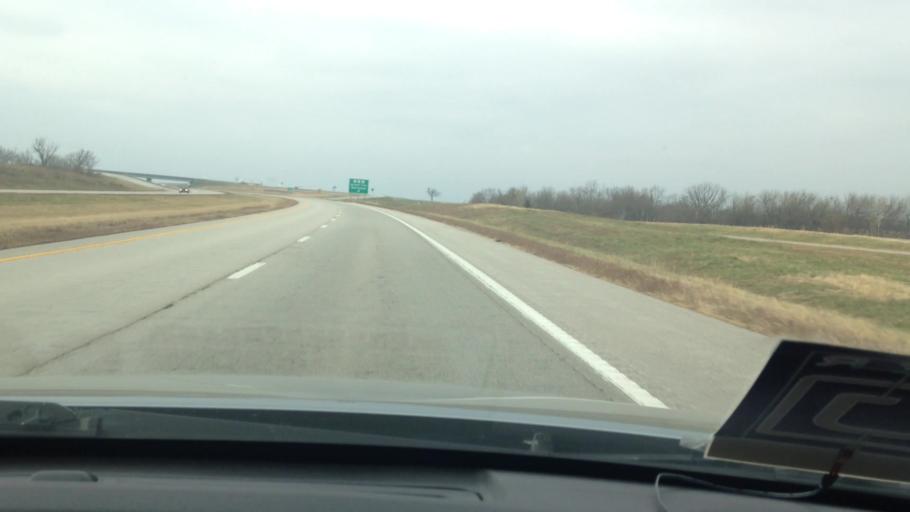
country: US
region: Missouri
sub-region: Cass County
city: Garden City
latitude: 38.5678
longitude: -94.1869
